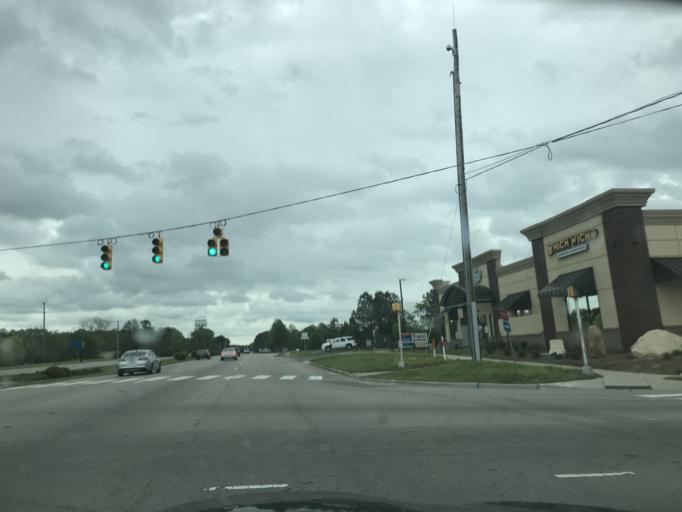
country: US
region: North Carolina
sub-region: Wake County
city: Knightdale
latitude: 35.7982
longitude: -78.4875
